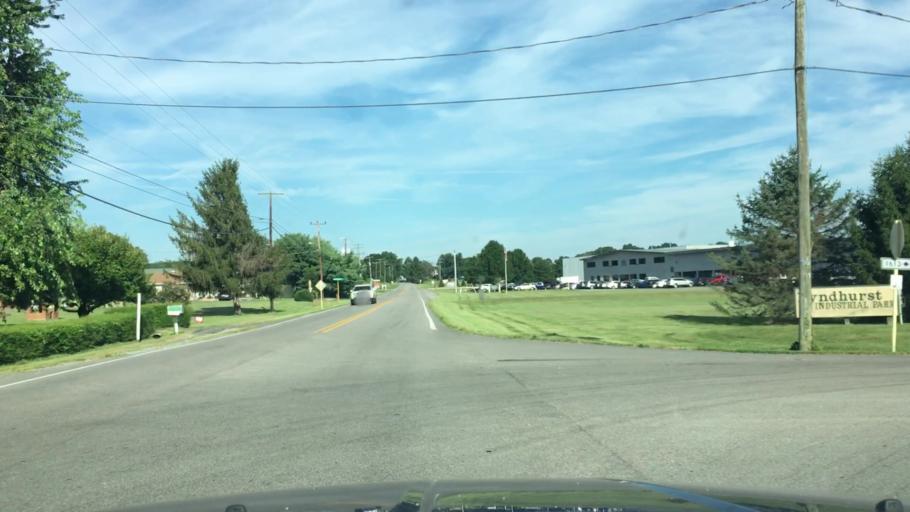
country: US
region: Virginia
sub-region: Augusta County
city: Lyndhurst
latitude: 38.0287
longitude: -78.9356
